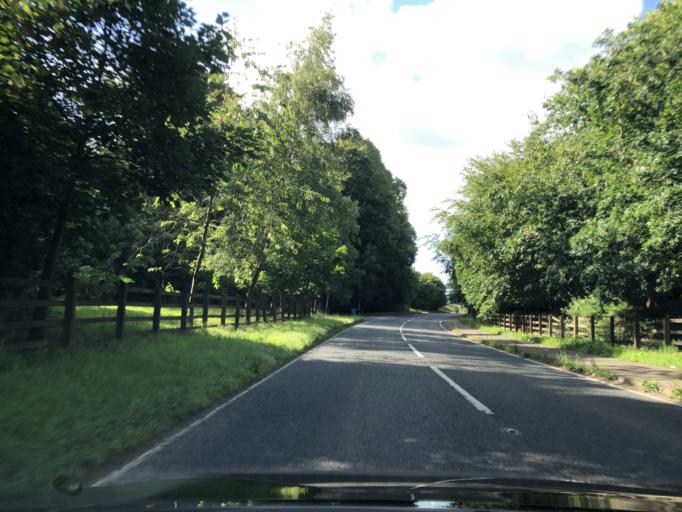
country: GB
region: Northern Ireland
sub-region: Ards District
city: Comber
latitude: 54.5644
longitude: -5.7664
